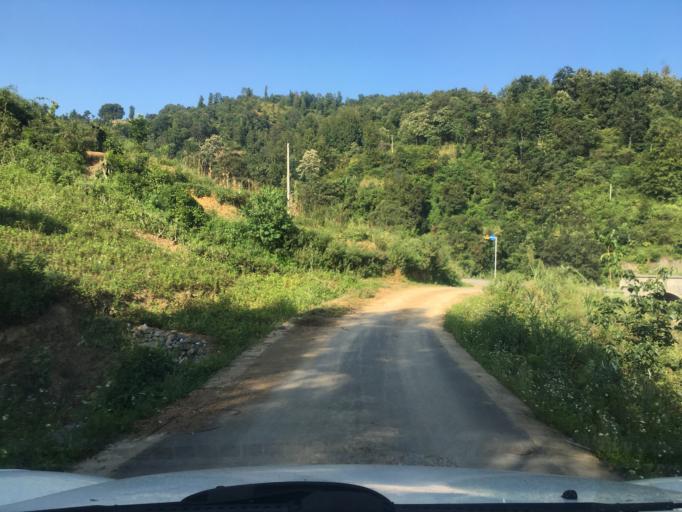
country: CN
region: Guangxi Zhuangzu Zizhiqu
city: Xinzhou
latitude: 25.4721
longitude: 105.7344
